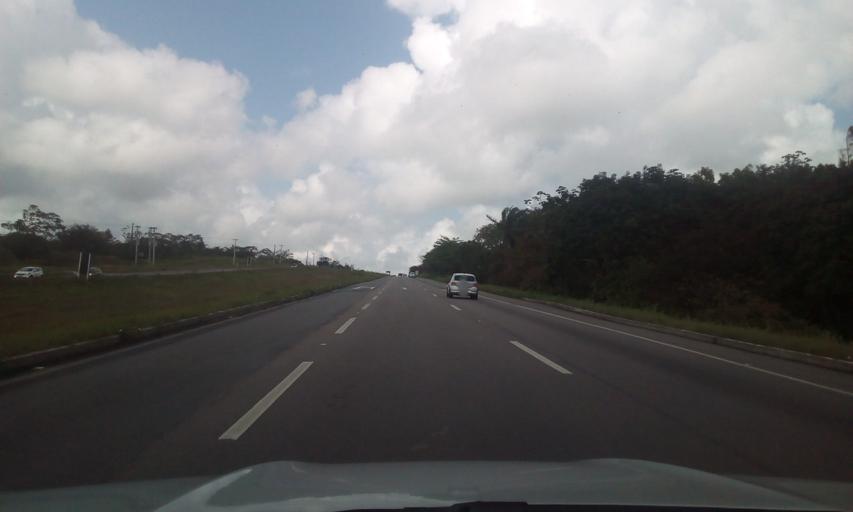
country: BR
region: Paraiba
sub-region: Alhandra
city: Alhandra
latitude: -7.4125
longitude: -34.9567
